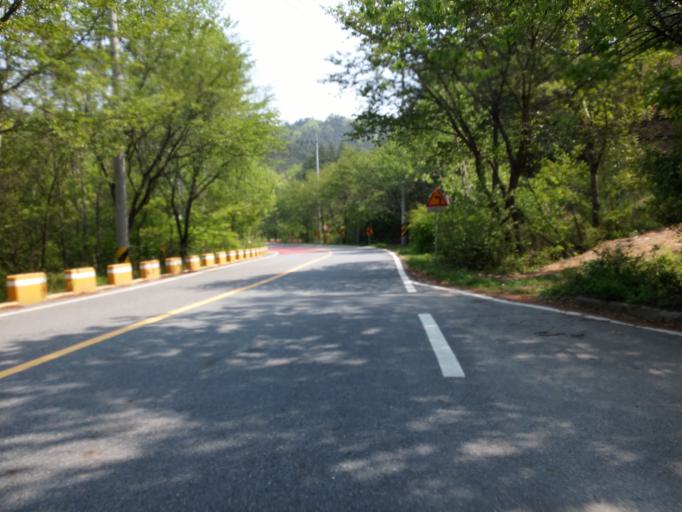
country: KR
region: Chungcheongbuk-do
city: Okcheon
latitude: 36.4002
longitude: 127.5355
